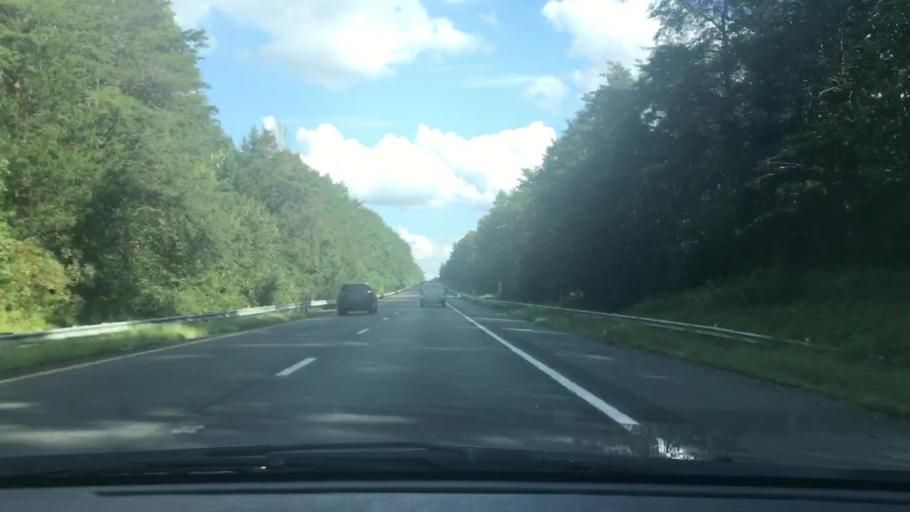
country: US
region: Virginia
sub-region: Louisa County
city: Louisa
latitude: 37.9251
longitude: -78.0835
